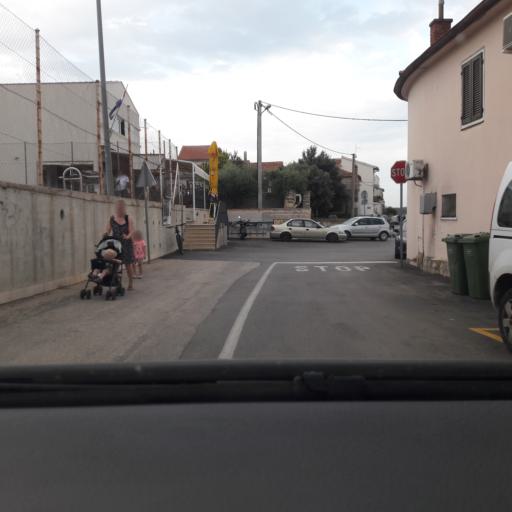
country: HR
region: Zadarska
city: Zadar
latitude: 44.1525
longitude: 15.2032
